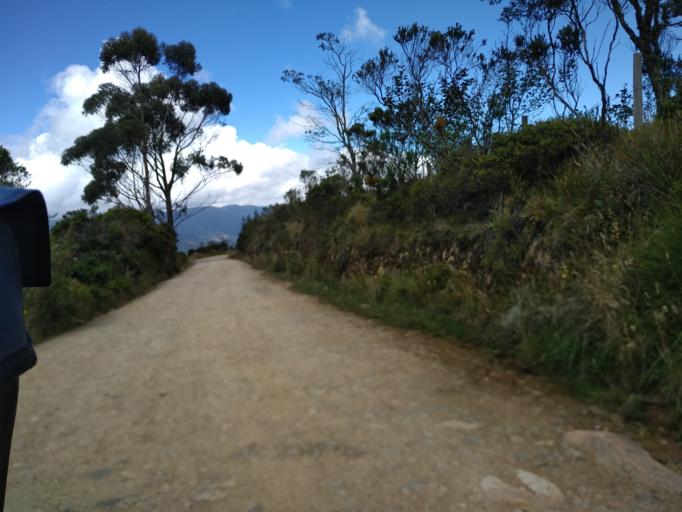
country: CO
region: Boyaca
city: Duitama
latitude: 5.9346
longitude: -73.1033
